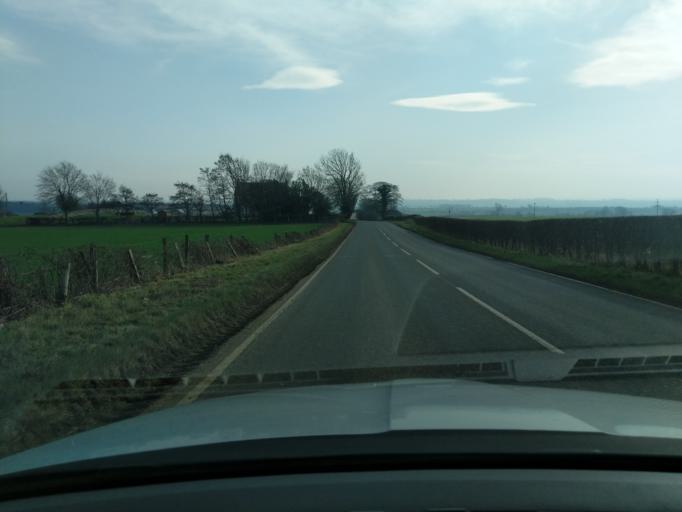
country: GB
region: England
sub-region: North Yorkshire
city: Catterick Garrison
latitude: 54.3390
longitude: -1.6871
